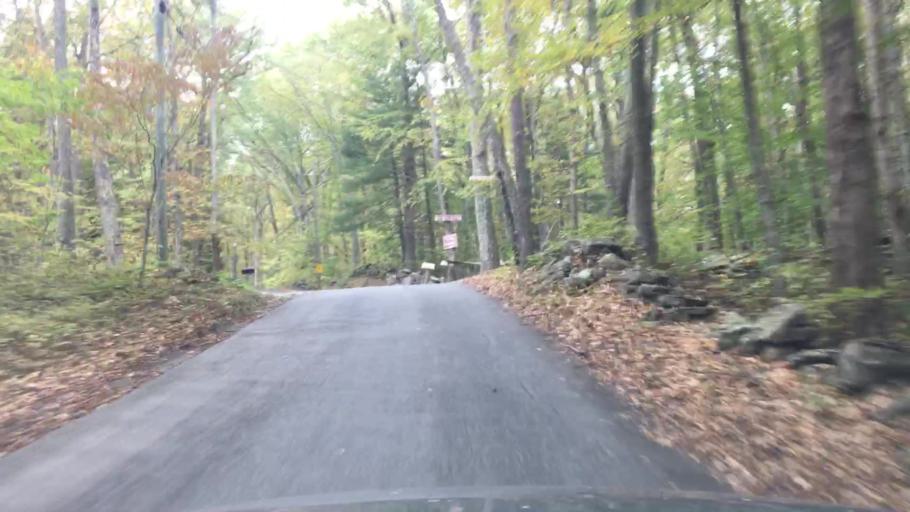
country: US
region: Connecticut
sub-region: Tolland County
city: Storrs
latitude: 41.8800
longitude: -72.1716
